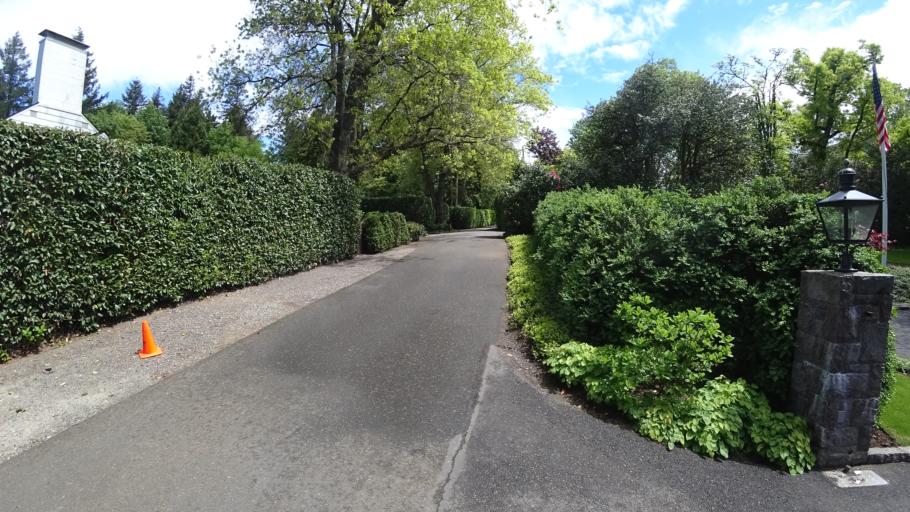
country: US
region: Oregon
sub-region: Washington County
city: West Slope
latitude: 45.5050
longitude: -122.7333
